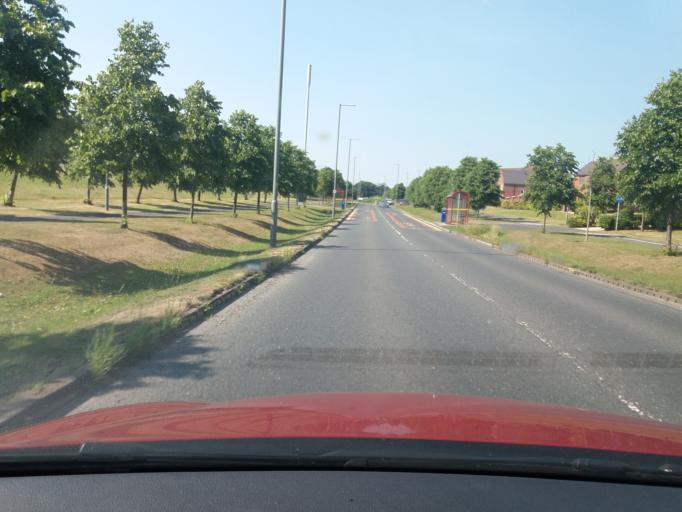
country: GB
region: England
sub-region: Lancashire
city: Clayton-le-Woods
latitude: 53.6832
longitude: -2.6642
